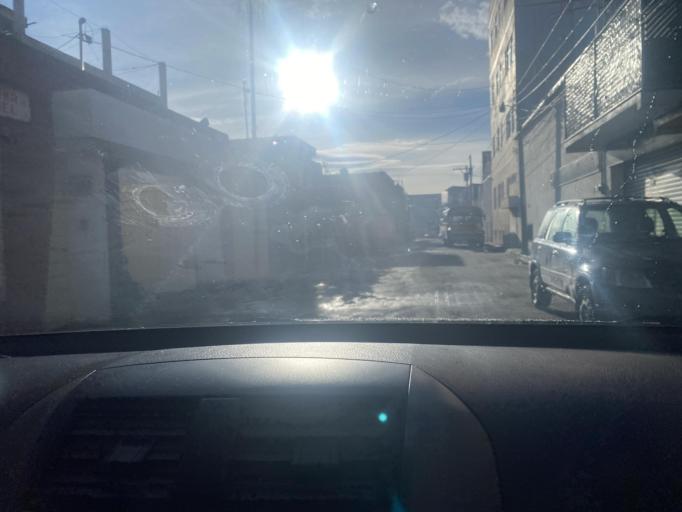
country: GT
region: Quetzaltenango
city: Olintepeque
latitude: 14.8600
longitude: -91.5219
